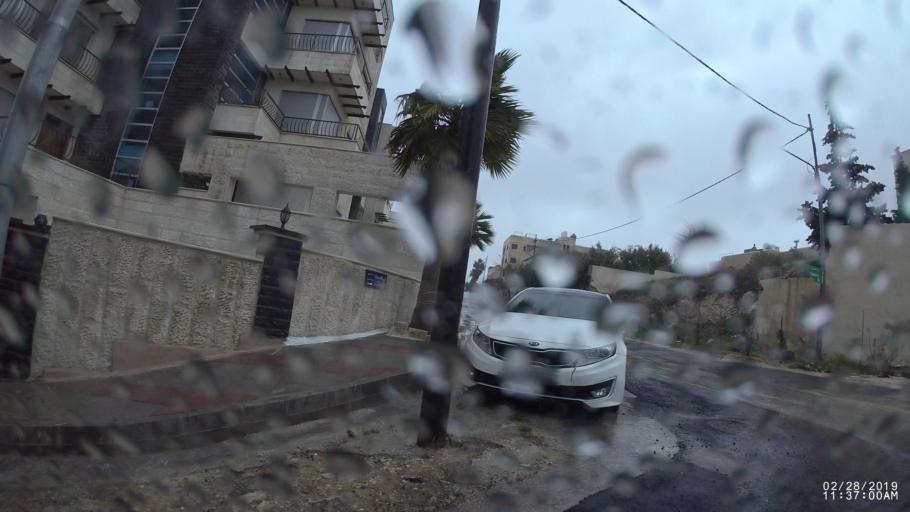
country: JO
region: Amman
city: Al Jubayhah
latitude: 32.0115
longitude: 35.8953
